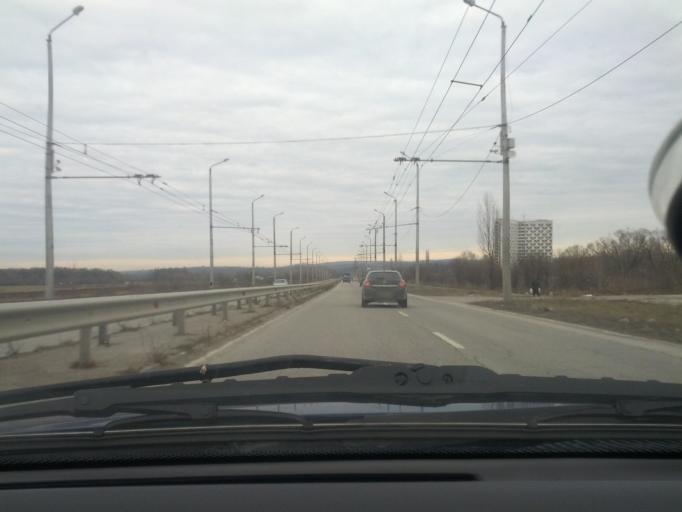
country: BG
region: Vratsa
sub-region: Obshtina Vratsa
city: Vratsa
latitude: 43.2302
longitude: 23.5627
